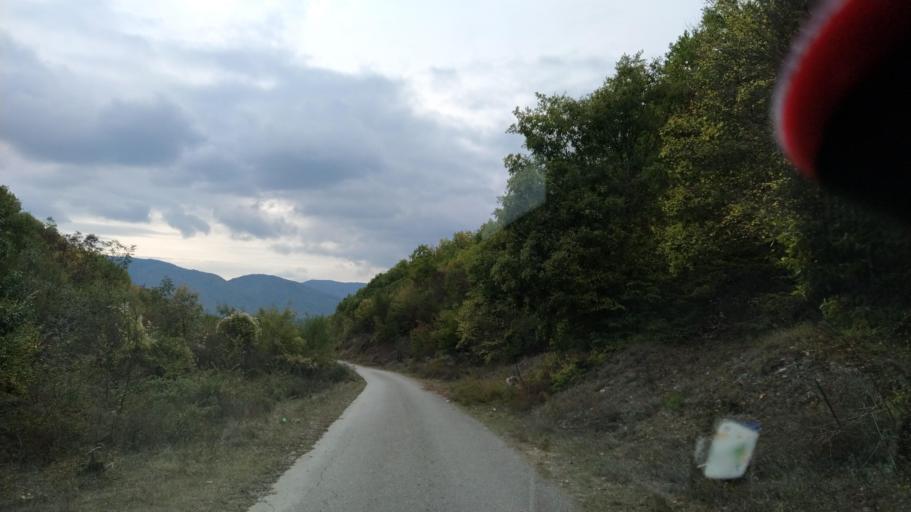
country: MK
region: Strumica
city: Veljusa
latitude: 41.5099
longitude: 22.4794
